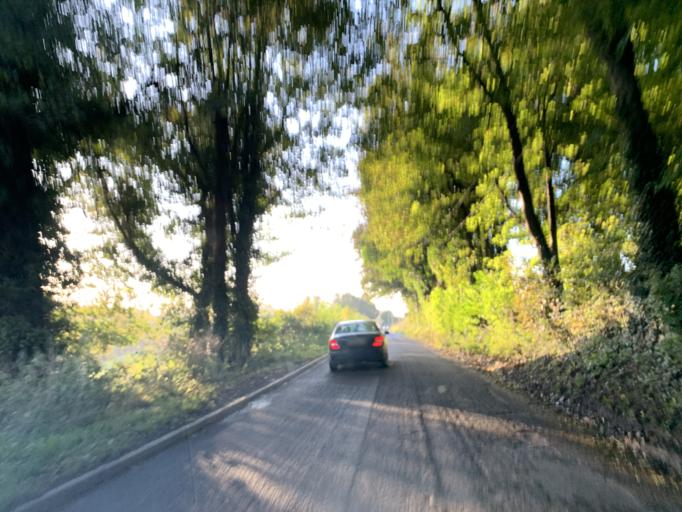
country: GB
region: England
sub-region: Wiltshire
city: Woodford
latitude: 51.1026
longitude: -1.8267
